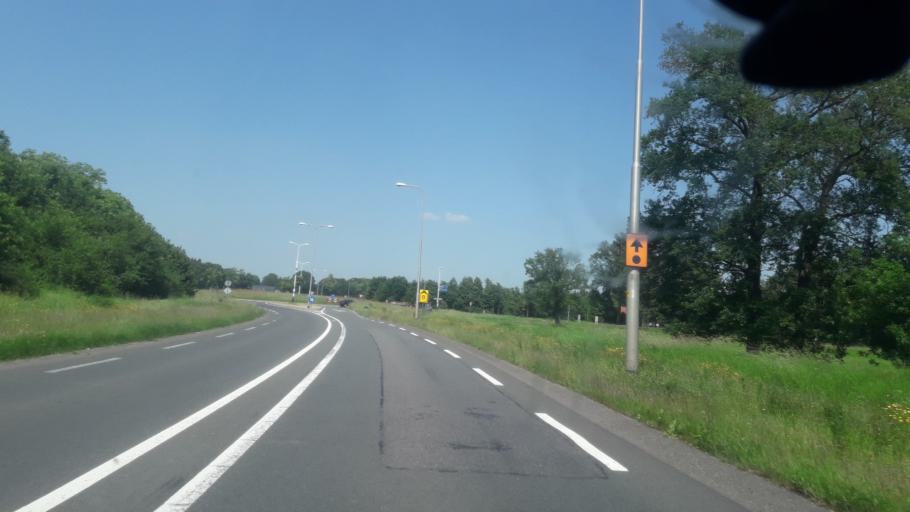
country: NL
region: Overijssel
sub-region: Gemeente Deventer
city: Schalkhaar
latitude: 52.2819
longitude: 6.2199
